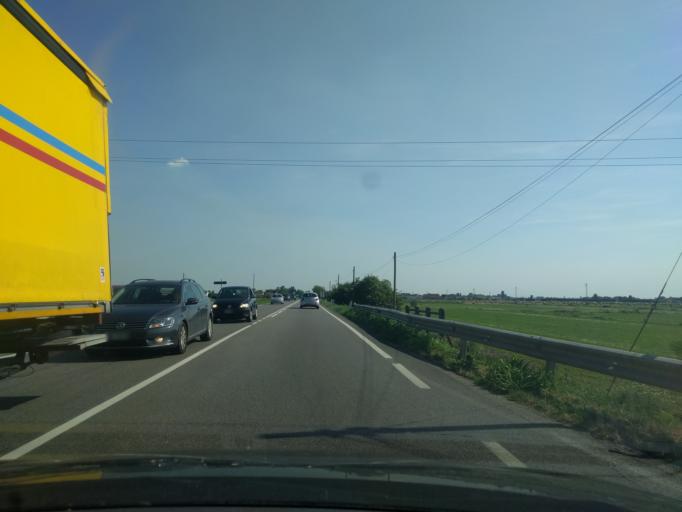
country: IT
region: Veneto
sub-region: Provincia di Padova
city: Solesino
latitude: 45.1692
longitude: 11.7564
